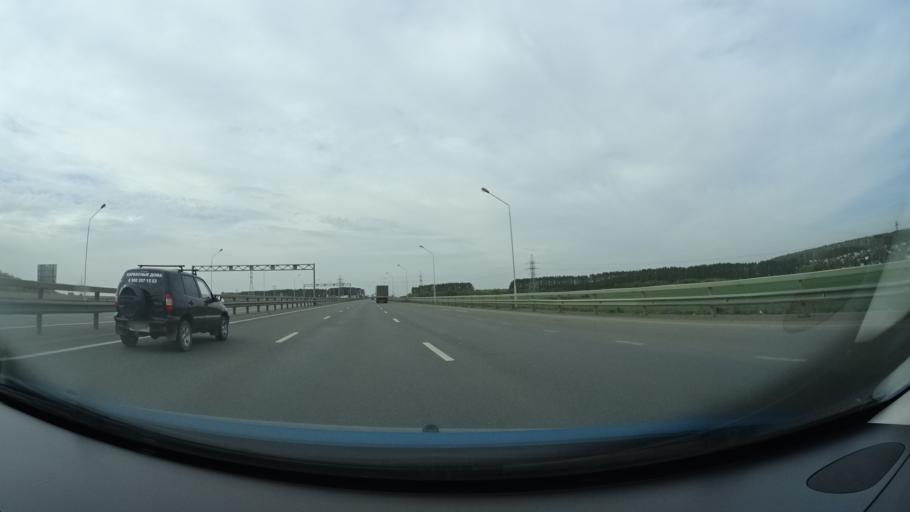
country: RU
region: Bashkortostan
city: Avdon
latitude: 54.6759
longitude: 55.7969
